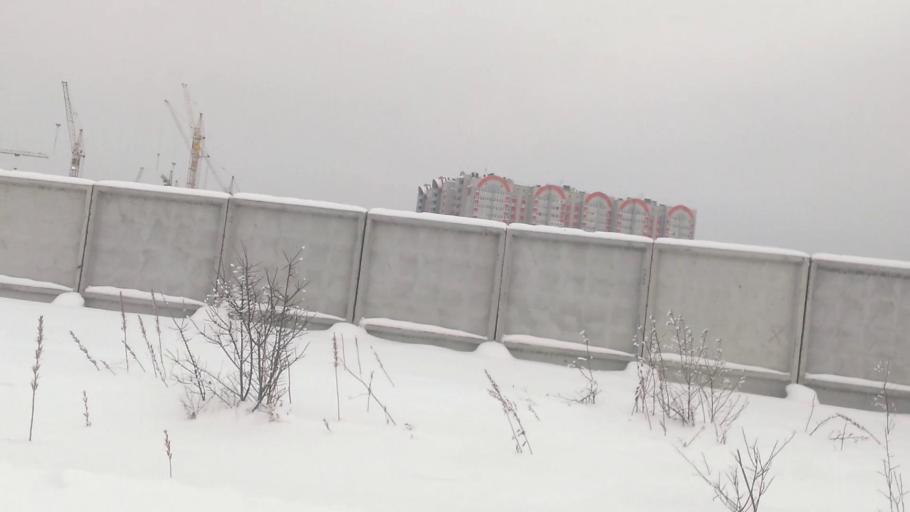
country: RU
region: Altai Krai
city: Novosilikatnyy
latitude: 53.3523
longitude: 83.6609
